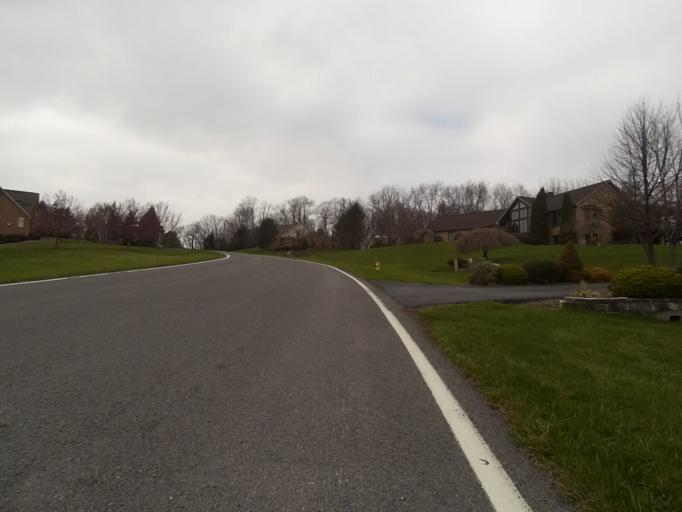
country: US
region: Pennsylvania
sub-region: Centre County
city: Boalsburg
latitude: 40.7926
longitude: -77.7603
